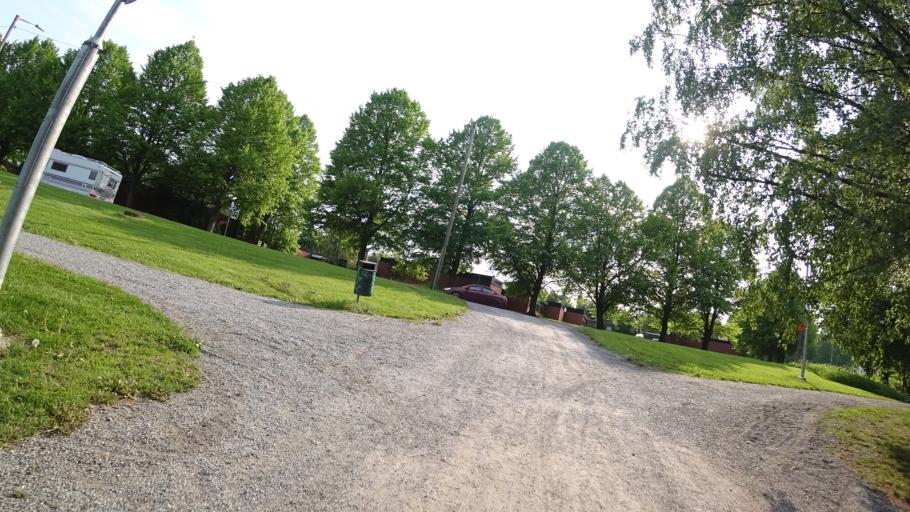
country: FI
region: Pirkanmaa
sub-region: Tampere
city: Pirkkala
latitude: 61.5029
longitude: 23.6620
